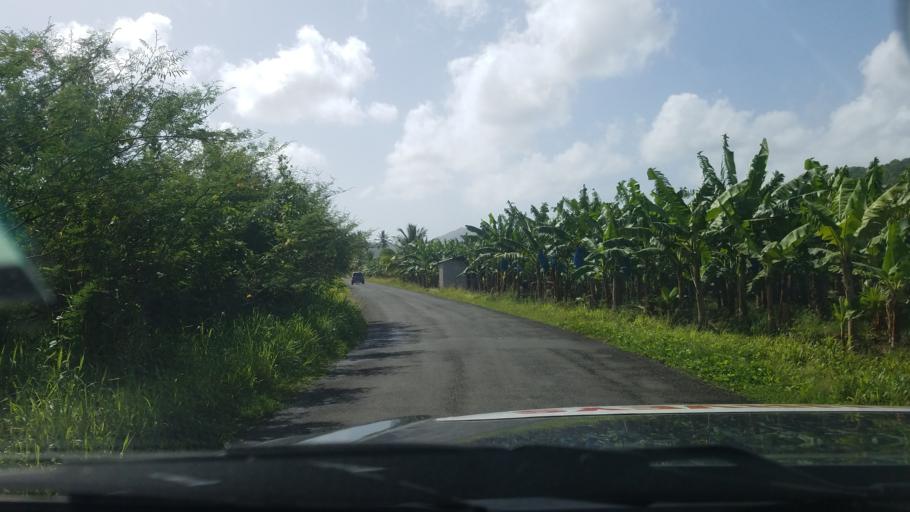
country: LC
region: Anse-la-Raye
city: Anse La Raye
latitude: 13.9569
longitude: -61.0170
